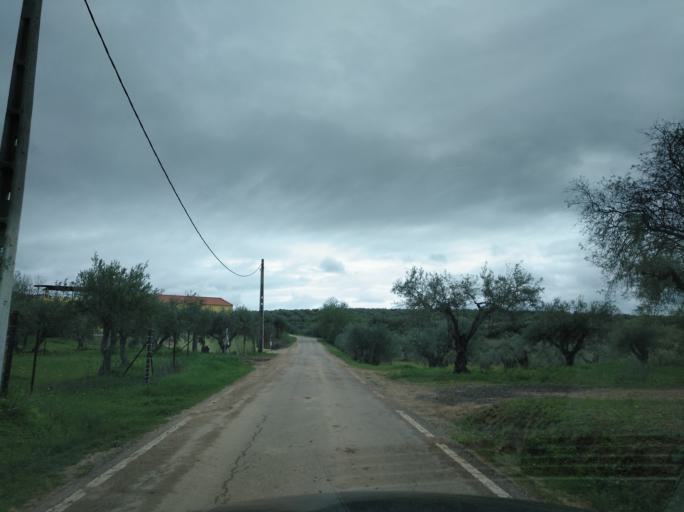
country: PT
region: Portalegre
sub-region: Campo Maior
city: Campo Maior
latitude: 38.9892
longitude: -7.0458
